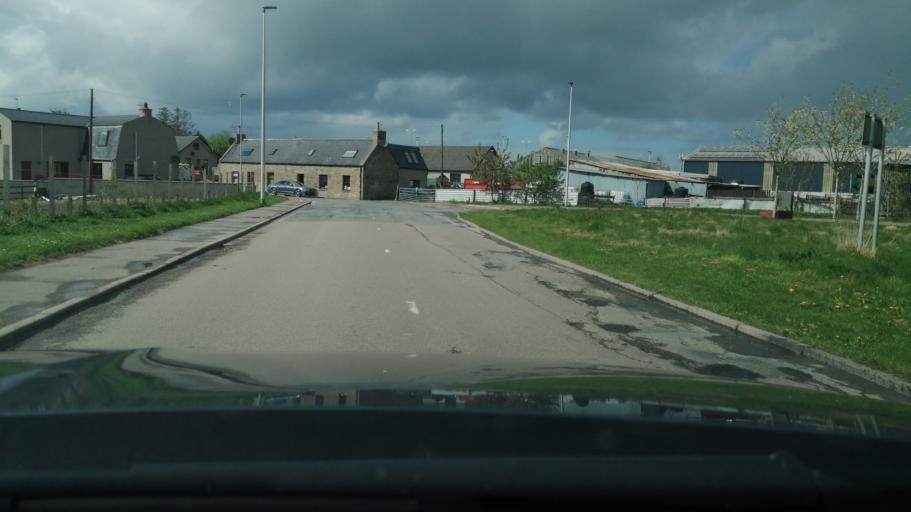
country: GB
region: Scotland
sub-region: Moray
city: Keith
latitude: 57.5376
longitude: -2.9444
